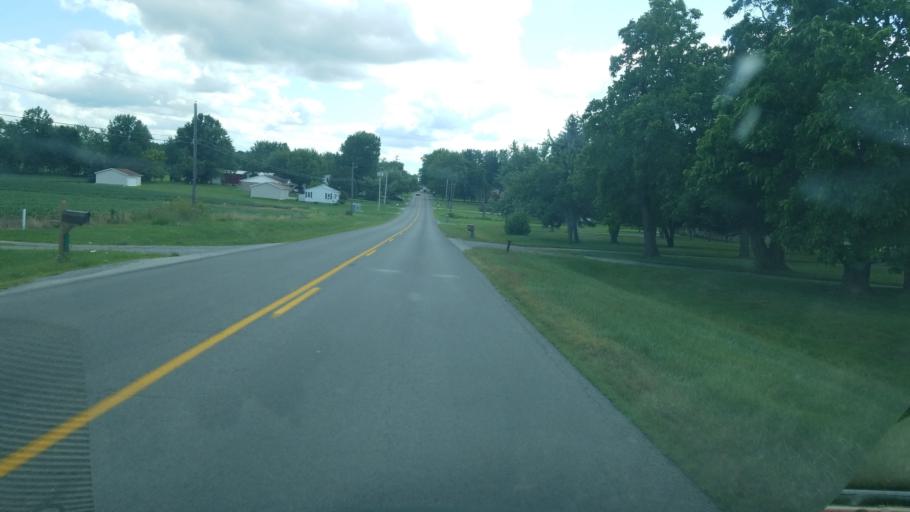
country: US
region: Ohio
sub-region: Allen County
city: Lima
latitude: 40.7692
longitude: -84.0705
